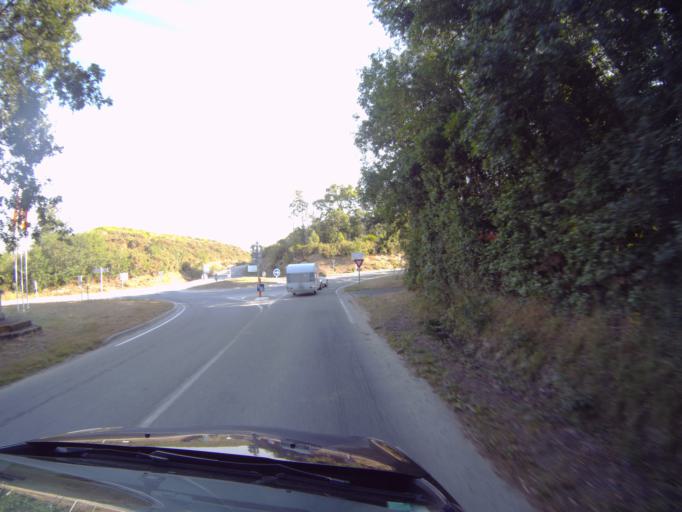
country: FR
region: Pays de la Loire
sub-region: Departement de la Vendee
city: Saint-Hilaire-de-Talmont
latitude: 46.4742
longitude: -1.6045
